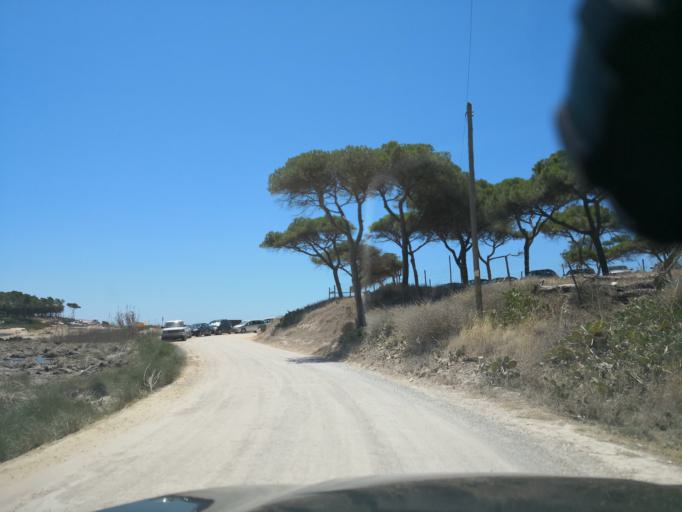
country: PT
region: Faro
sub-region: Loule
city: Quarteira
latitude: 37.0602
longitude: -8.0839
